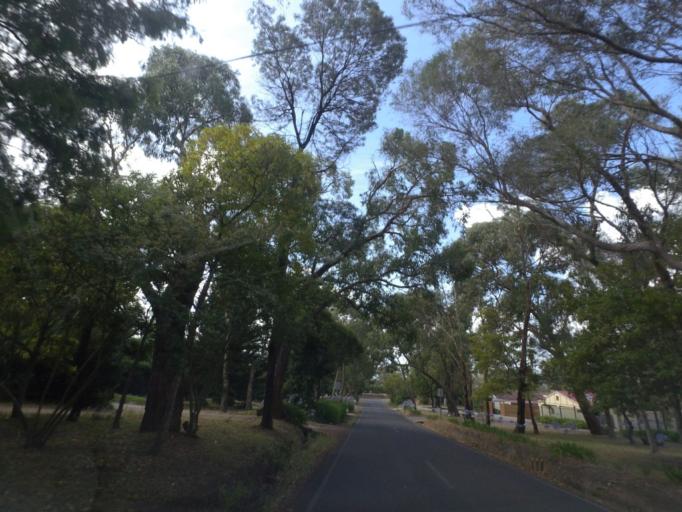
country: AU
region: Victoria
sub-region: Yarra Ranges
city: Lilydale
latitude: -37.7785
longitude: 145.3506
